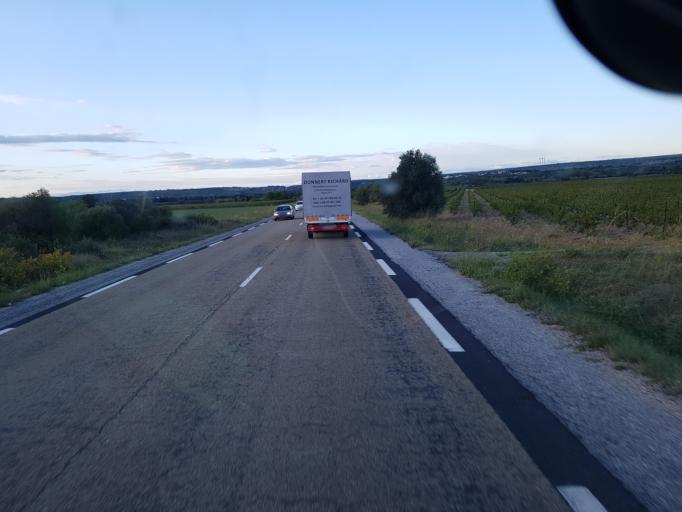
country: FR
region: Languedoc-Roussillon
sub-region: Departement de l'Aude
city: Leucate
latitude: 42.9500
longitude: 2.9872
